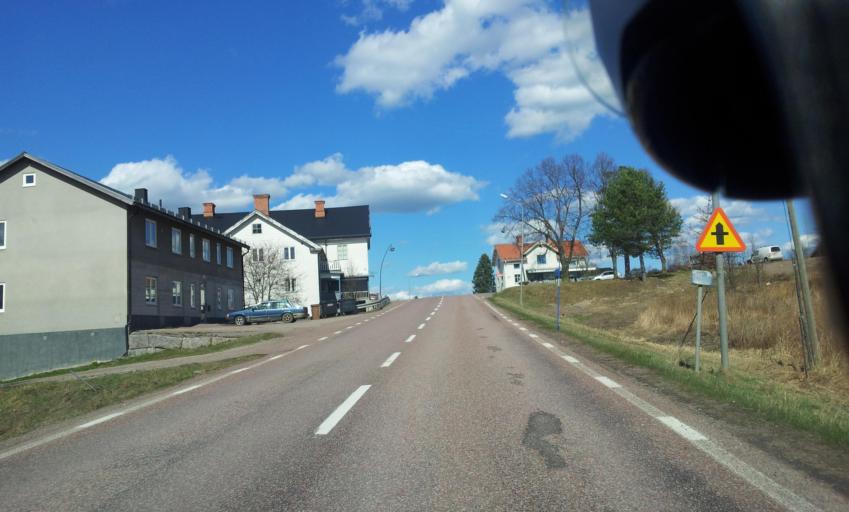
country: SE
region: Dalarna
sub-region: Faluns Kommun
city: Svardsjo
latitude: 60.8069
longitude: 15.7574
